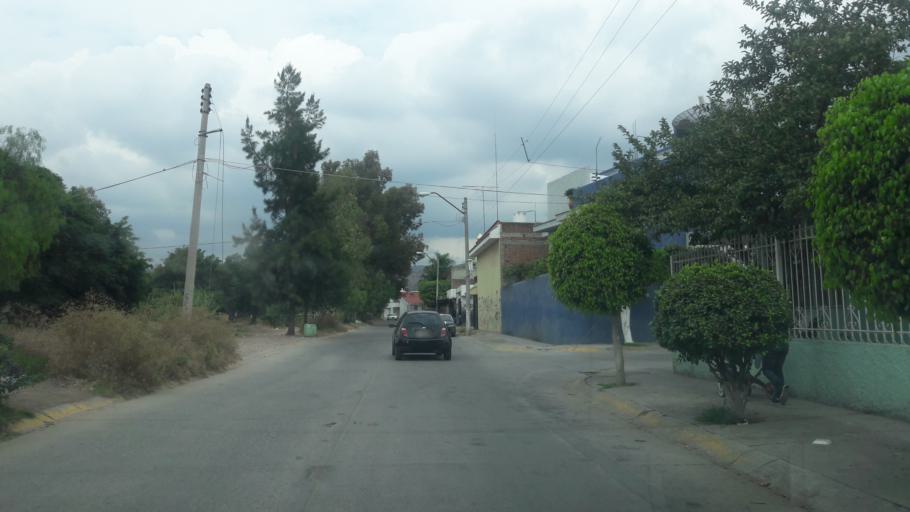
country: MX
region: Guanajuato
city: Leon
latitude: 21.1789
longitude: -101.6690
